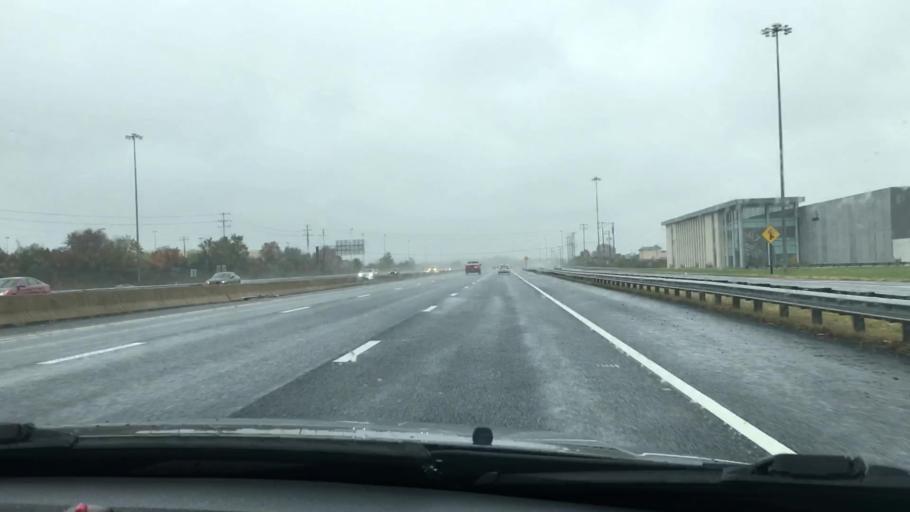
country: US
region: Virginia
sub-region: Loudoun County
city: Dulles Town Center
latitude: 39.0267
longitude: -77.4315
